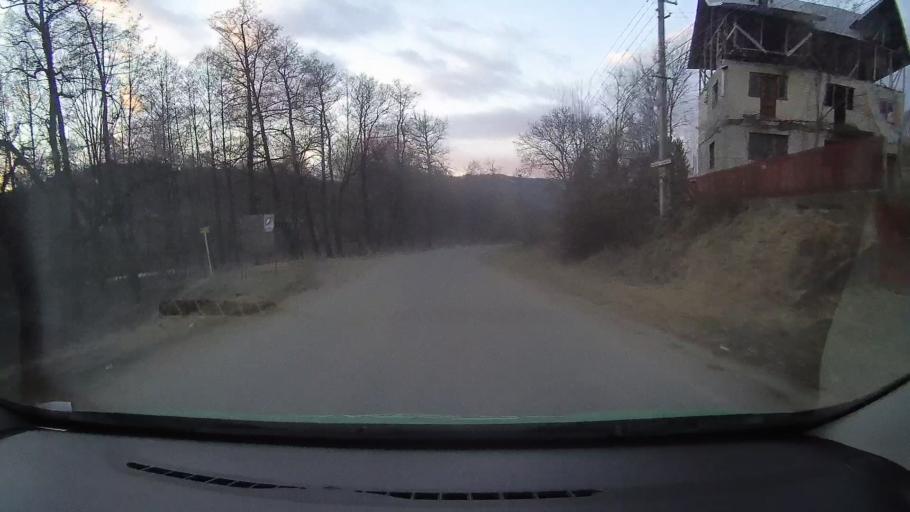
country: RO
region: Dambovita
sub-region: Comuna Valea Lunga
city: Valea Lunga-Cricov
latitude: 45.0702
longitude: 25.5800
